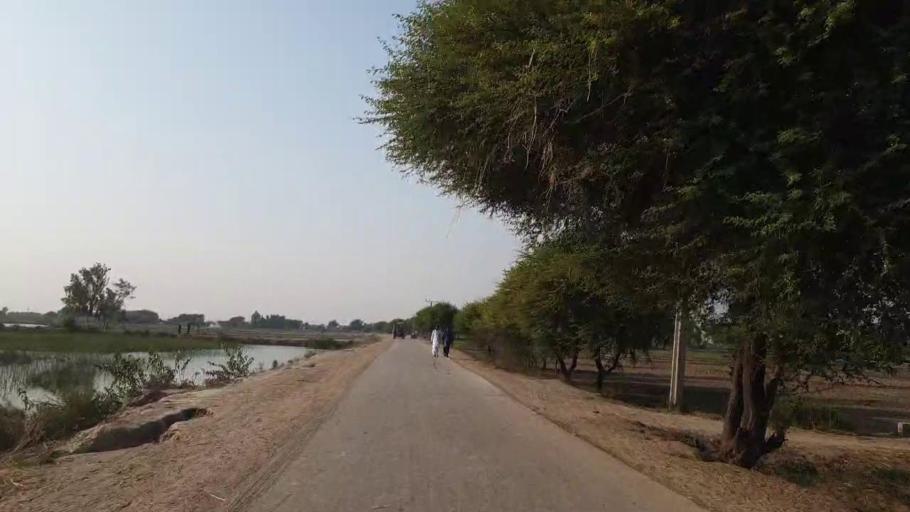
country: PK
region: Sindh
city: Bulri
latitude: 24.9955
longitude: 68.3826
